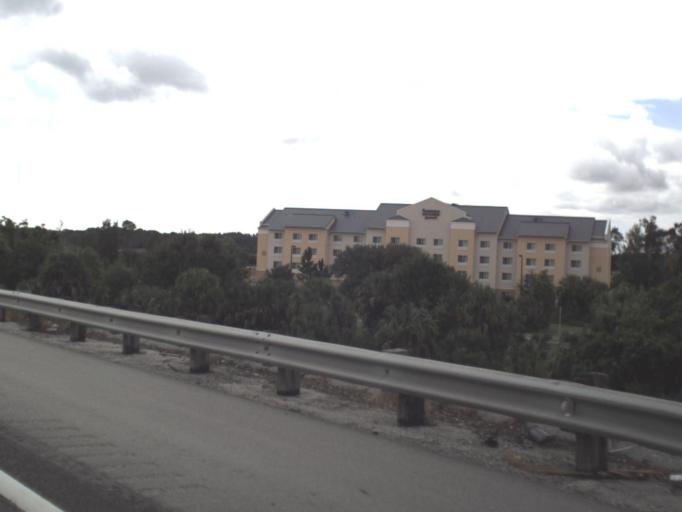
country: US
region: Florida
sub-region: Sarasota County
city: Plantation
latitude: 27.1107
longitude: -82.3838
